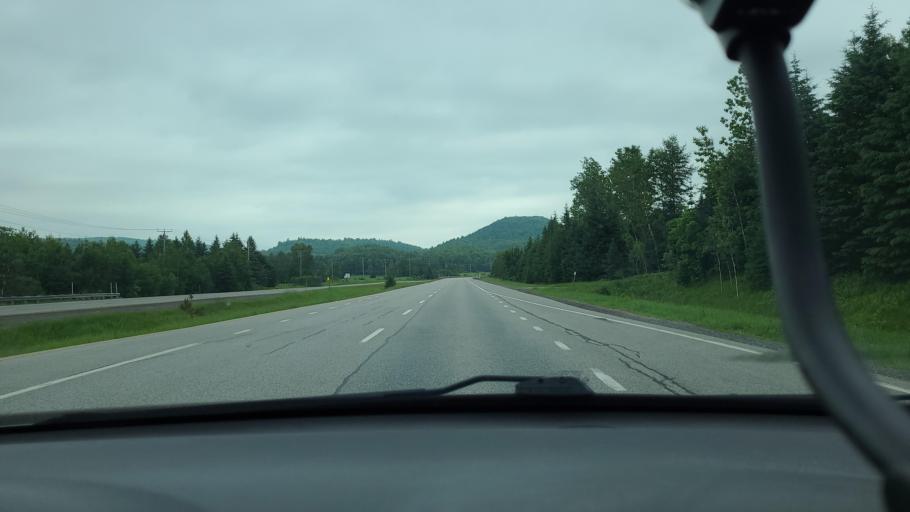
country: CA
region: Quebec
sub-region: Laurentides
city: Labelle
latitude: 46.1820
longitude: -74.7286
